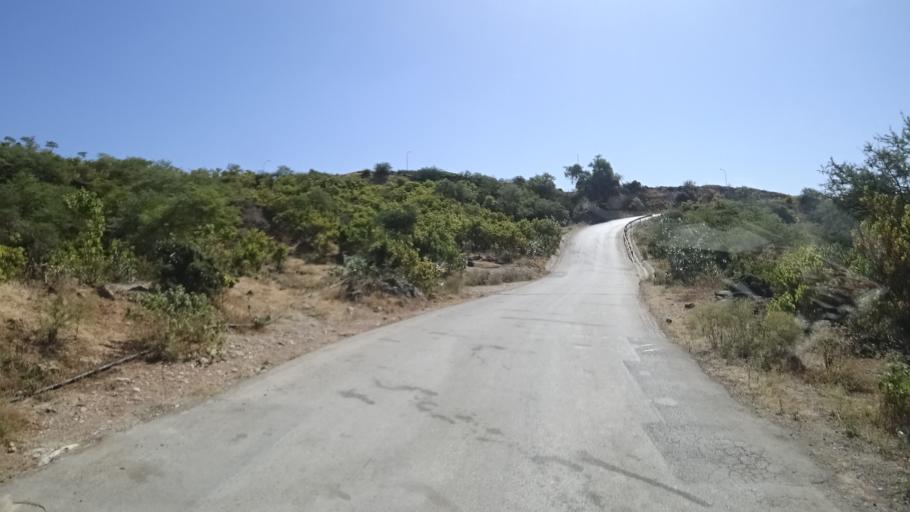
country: OM
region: Zufar
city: Salalah
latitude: 17.0714
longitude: 54.4458
